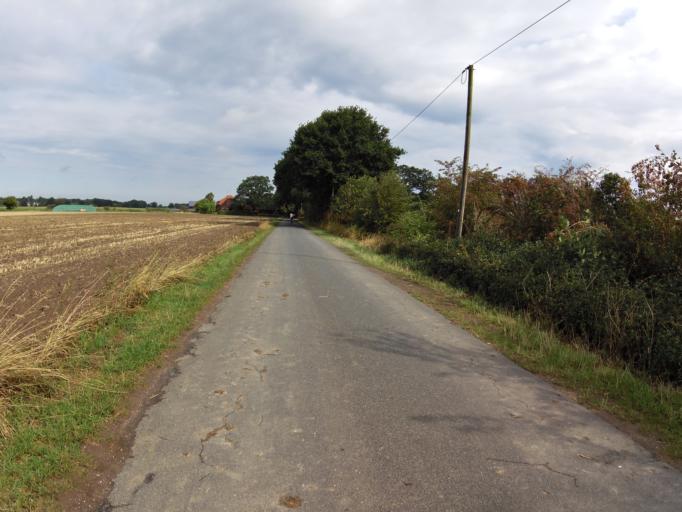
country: DE
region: Lower Saxony
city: Marklohe
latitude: 52.6774
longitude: 9.1711
